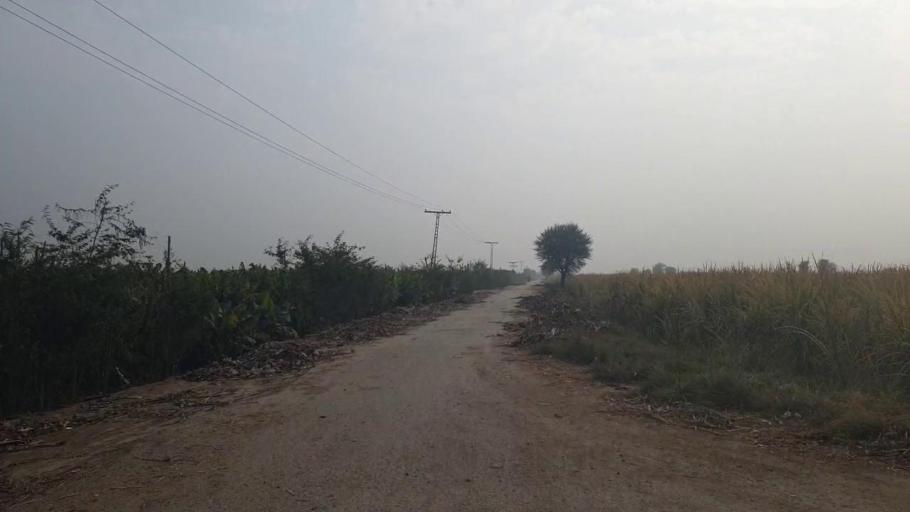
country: PK
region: Sindh
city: Berani
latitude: 25.8074
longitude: 68.7329
